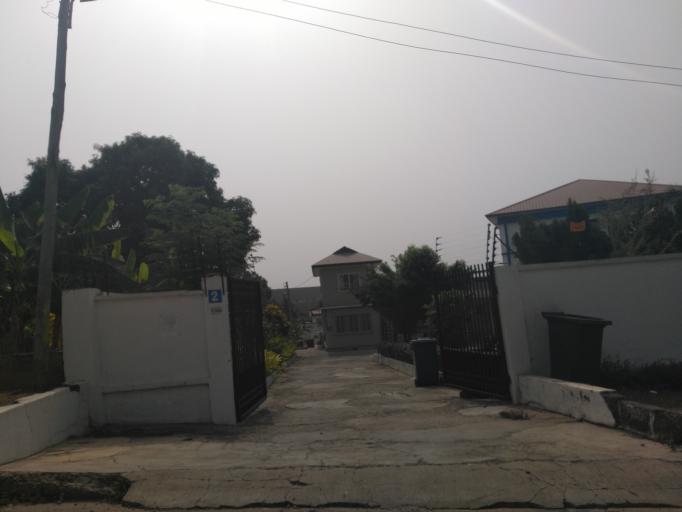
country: GH
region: Ashanti
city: Kumasi
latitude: 6.6755
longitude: -1.6069
